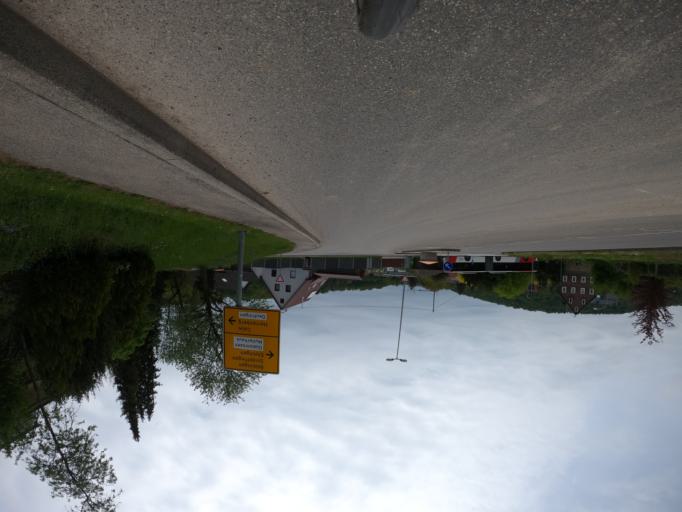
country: DE
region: Baden-Wuerttemberg
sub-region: Regierungsbezirk Stuttgart
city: Aidlingen
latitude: 48.6797
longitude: 8.9048
